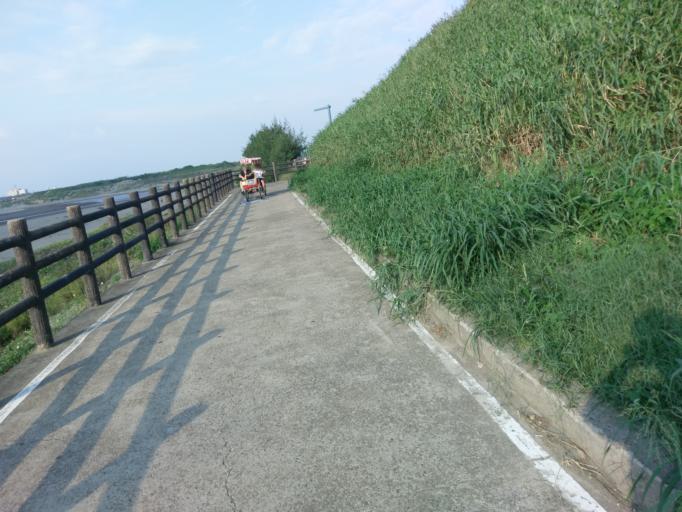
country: TW
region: Taiwan
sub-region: Hsinchu
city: Hsinchu
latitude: 24.8368
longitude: 120.9175
